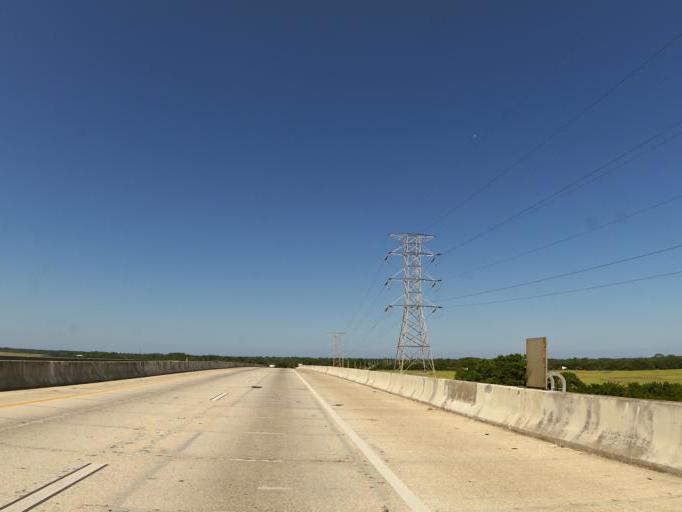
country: US
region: Florida
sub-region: Nassau County
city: Fernandina Beach
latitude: 30.6277
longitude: -81.4837
